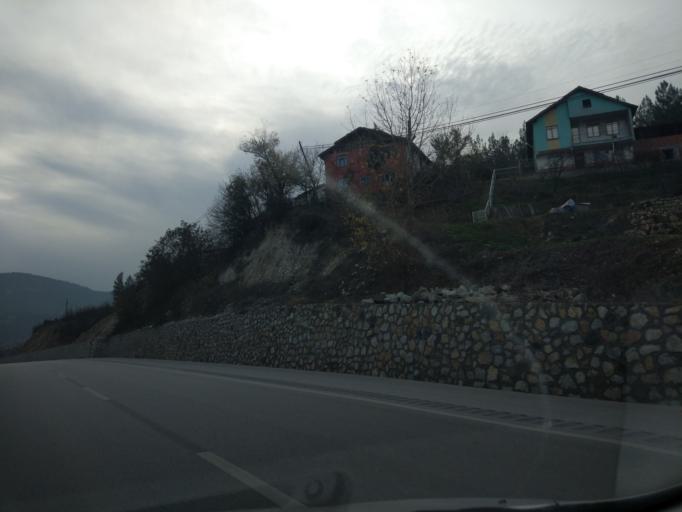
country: TR
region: Karabuk
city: Karabuk
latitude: 41.1120
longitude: 32.6697
